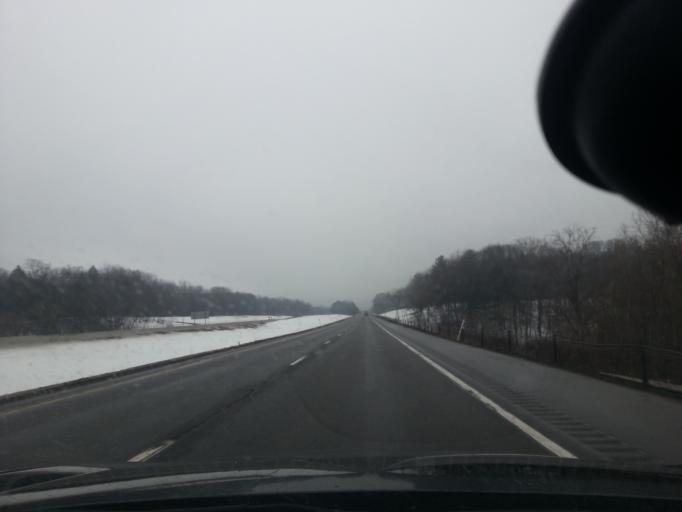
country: US
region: New York
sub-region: Jefferson County
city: Adams
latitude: 43.7055
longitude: -76.0756
